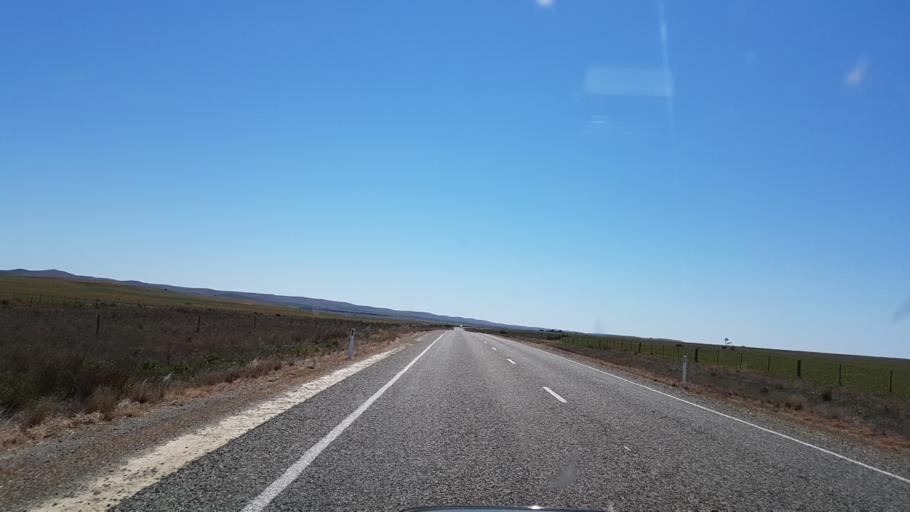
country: AU
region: South Australia
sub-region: Northern Areas
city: Jamestown
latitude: -33.2784
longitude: 138.8687
